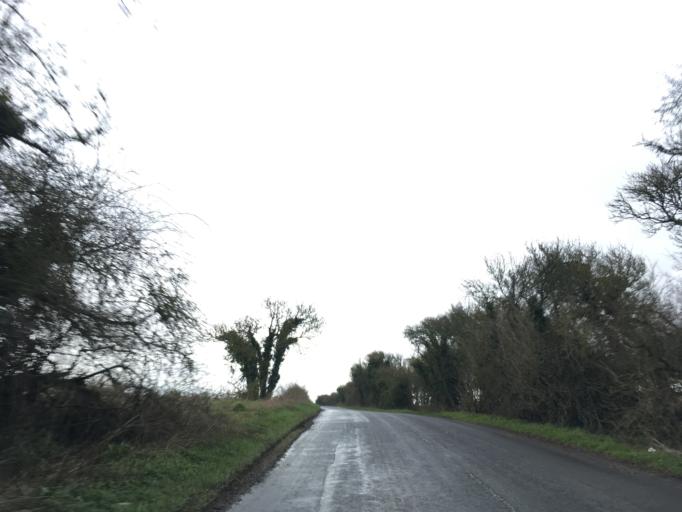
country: GB
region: England
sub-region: Borough of Swindon
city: Wanborough
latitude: 51.5436
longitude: -1.6864
